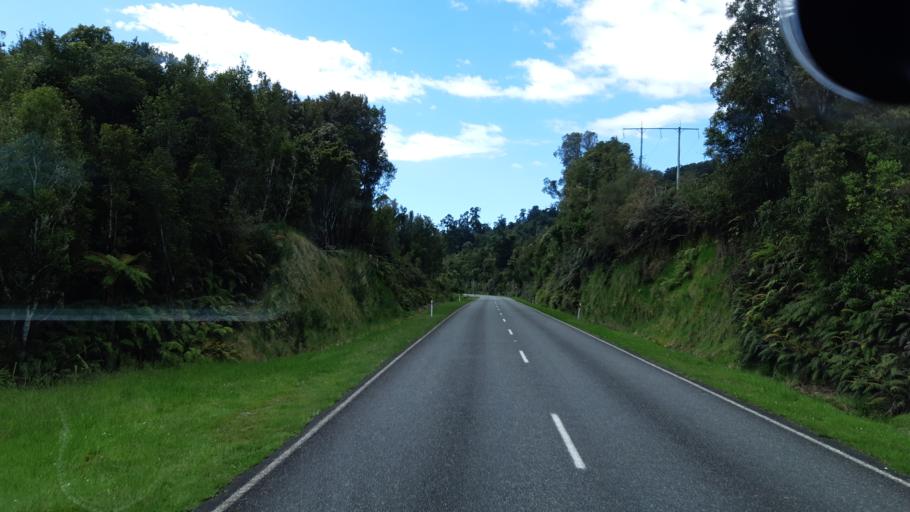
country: NZ
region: West Coast
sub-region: Westland District
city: Hokitika
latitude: -43.0532
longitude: 170.6373
